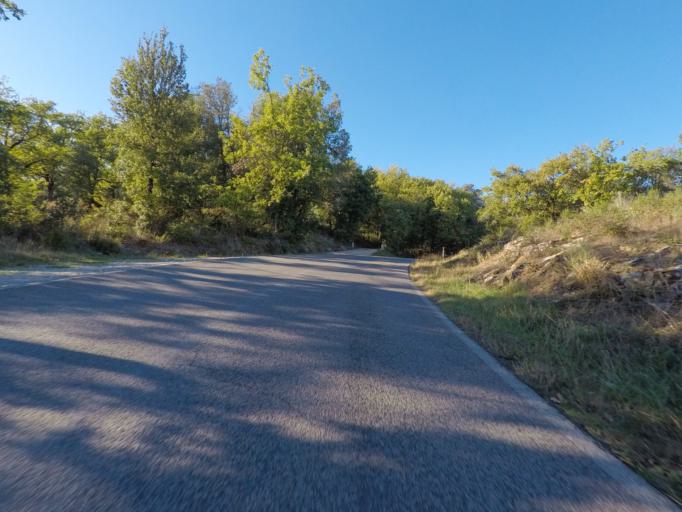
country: IT
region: Tuscany
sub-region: Provincia di Siena
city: Belverde
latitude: 43.4070
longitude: 11.3516
